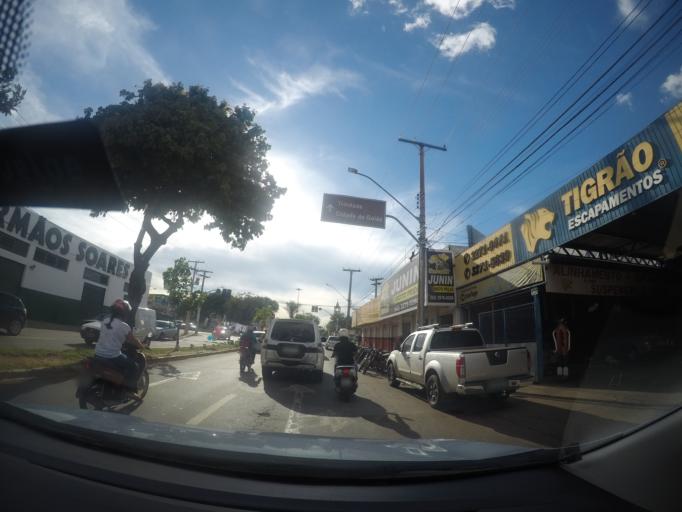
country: BR
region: Goias
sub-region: Goiania
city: Goiania
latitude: -16.6718
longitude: -49.3046
